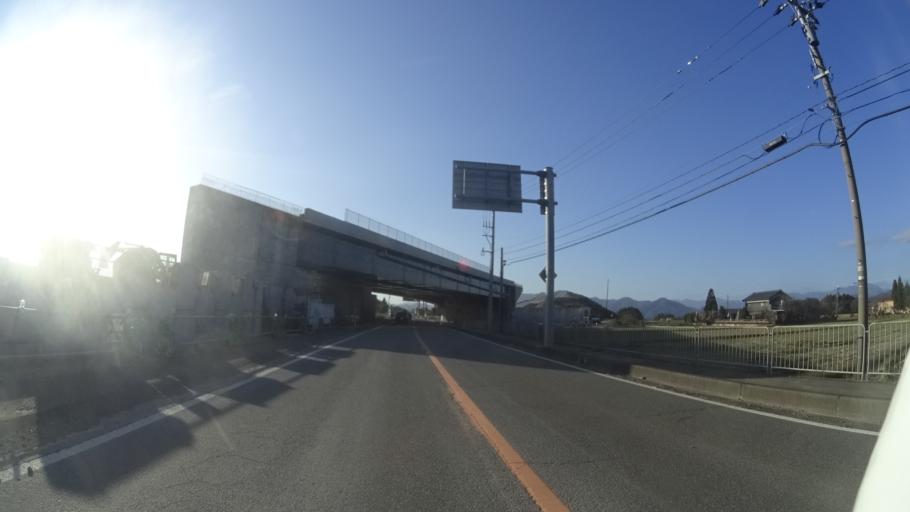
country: JP
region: Fukui
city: Ono
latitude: 35.9737
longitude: 136.5553
